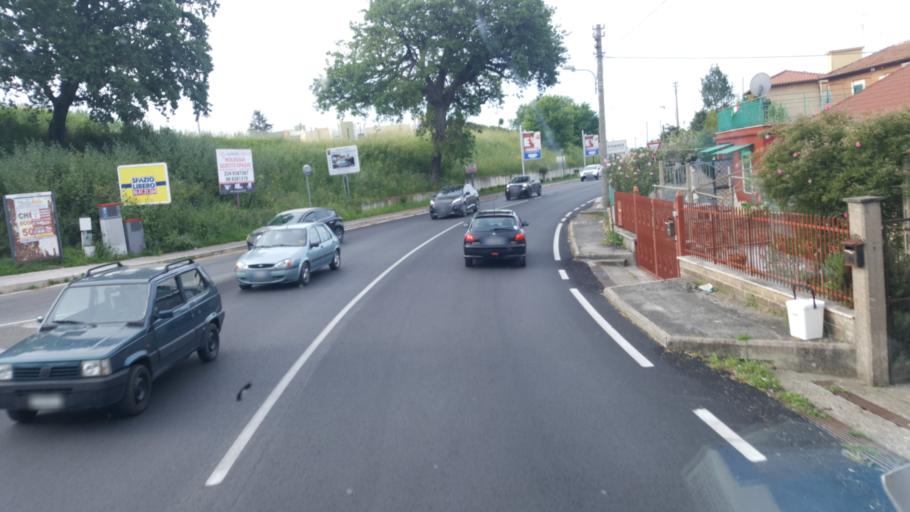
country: IT
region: Latium
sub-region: Citta metropolitana di Roma Capitale
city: Cecchina
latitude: 41.7017
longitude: 12.6475
